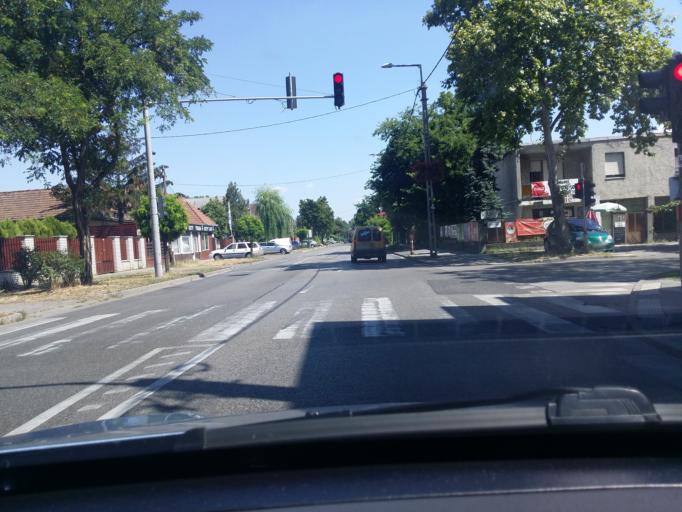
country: HU
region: Budapest
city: Budapest IV. keruelet
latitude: 47.5749
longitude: 19.0985
